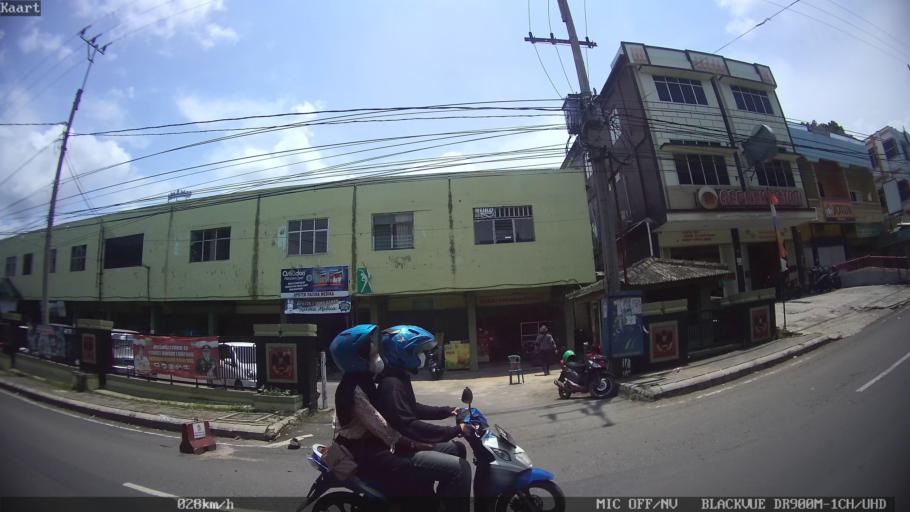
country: ID
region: Lampung
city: Kedaton
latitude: -5.3918
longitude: 105.2616
